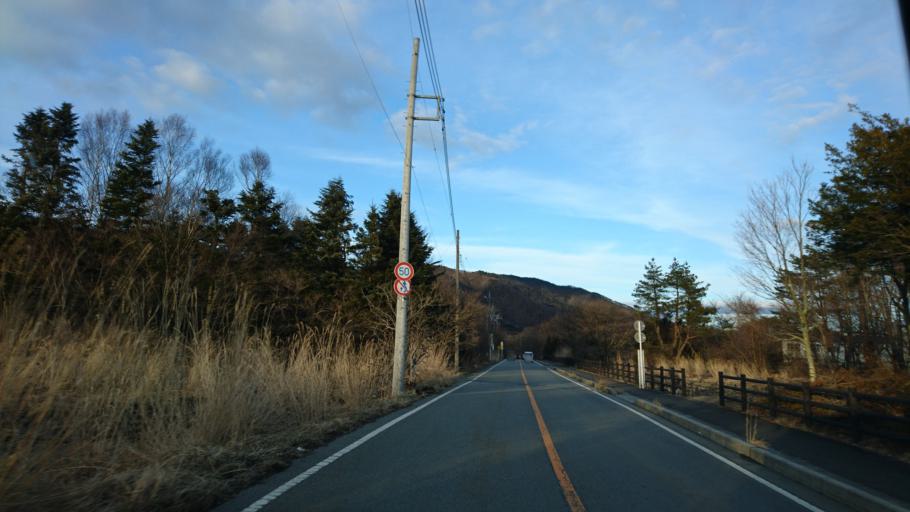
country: JP
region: Yamanashi
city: Fujikawaguchiko
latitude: 35.4749
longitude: 138.6778
